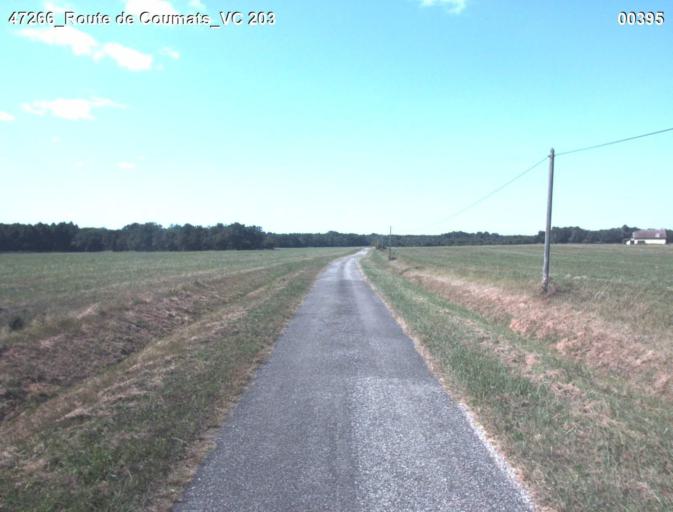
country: FR
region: Aquitaine
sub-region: Departement des Landes
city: Gabarret
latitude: 44.0142
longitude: 0.0898
